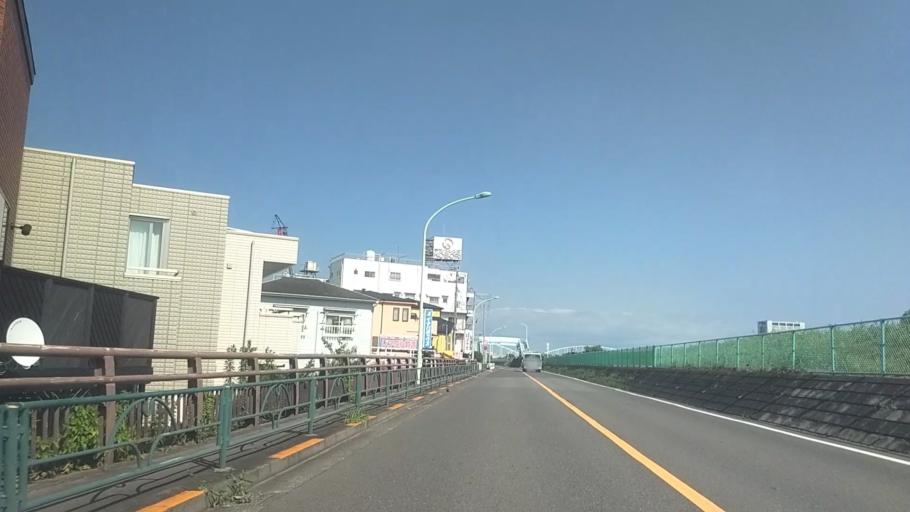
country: JP
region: Kanagawa
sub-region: Kawasaki-shi
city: Kawasaki
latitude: 35.5593
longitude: 139.6889
